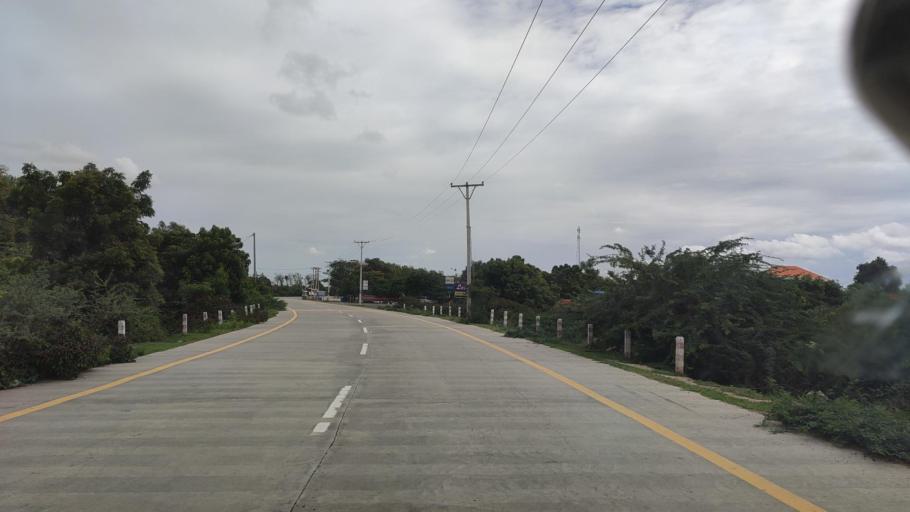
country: MM
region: Mandalay
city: Meiktila
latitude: 21.1233
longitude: 96.0274
